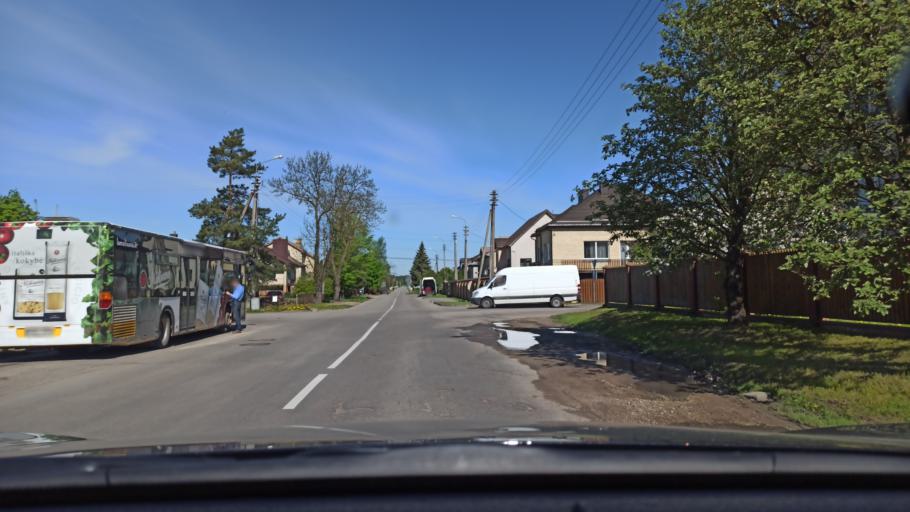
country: LT
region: Siauliu apskritis
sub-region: Siauliai
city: Siauliai
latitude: 55.9617
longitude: 23.2957
